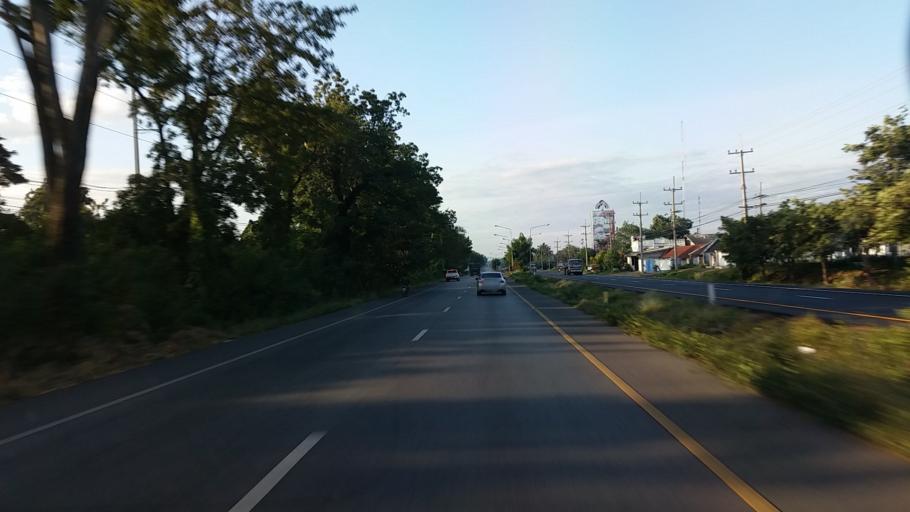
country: TH
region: Lop Buri
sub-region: Amphoe Tha Luang
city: Tha Luang
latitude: 15.1102
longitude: 101.0260
